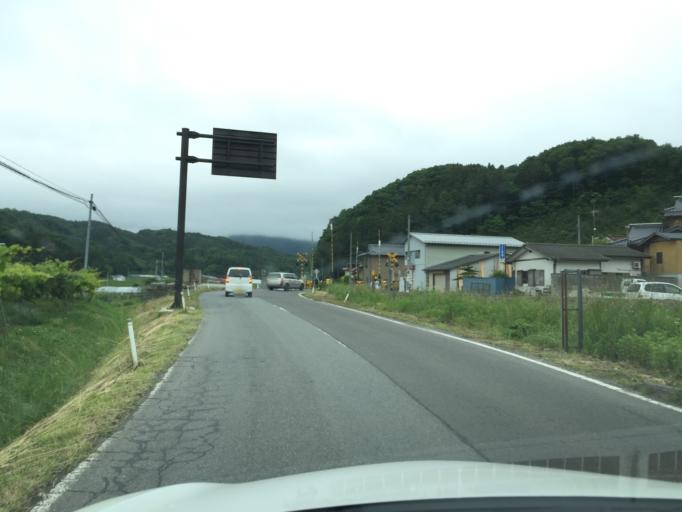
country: JP
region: Fukushima
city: Funehikimachi-funehiki
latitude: 37.3486
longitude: 140.6480
